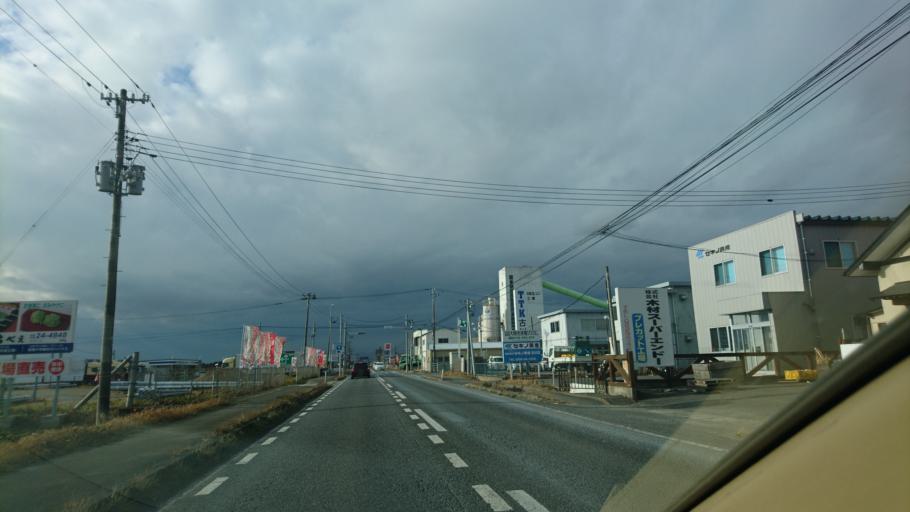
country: JP
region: Miyagi
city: Furukawa
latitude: 38.5669
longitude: 141.0003
